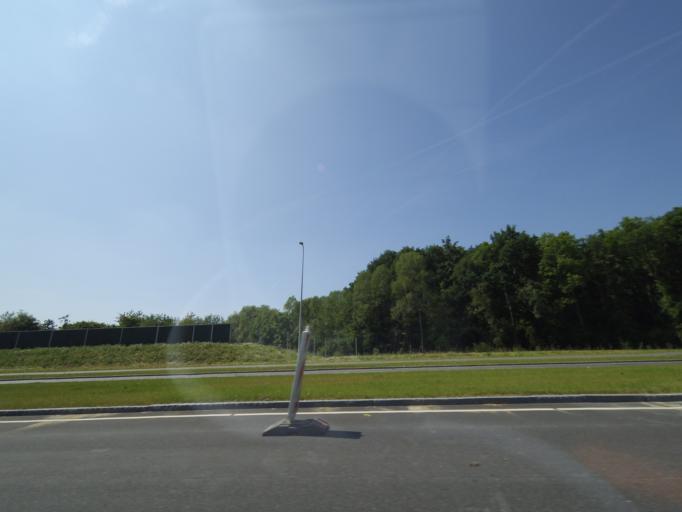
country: DK
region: South Denmark
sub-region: Odense Kommune
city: Hojby
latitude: 55.3670
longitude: 10.4112
